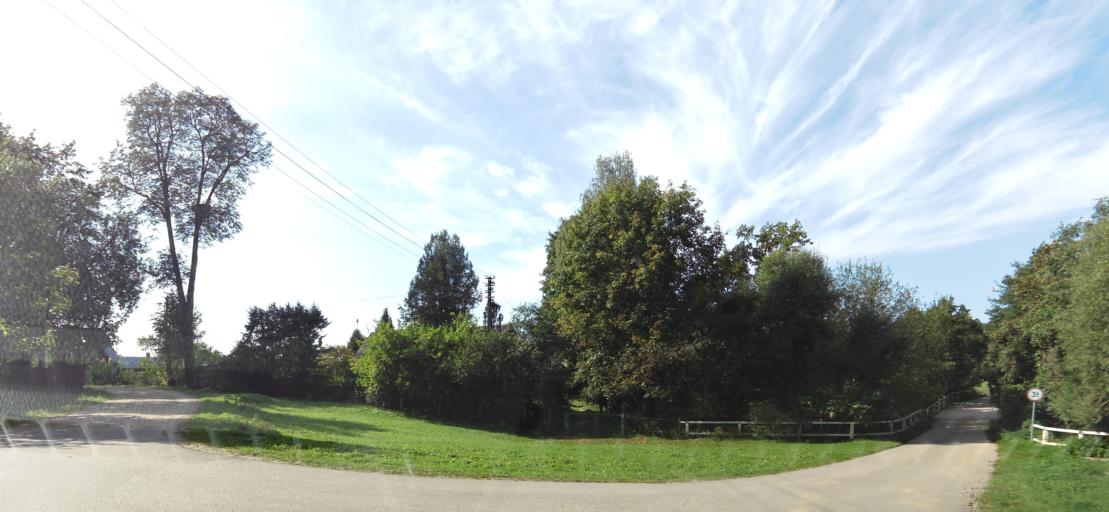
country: LT
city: Salcininkai
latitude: 54.4476
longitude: 25.5190
